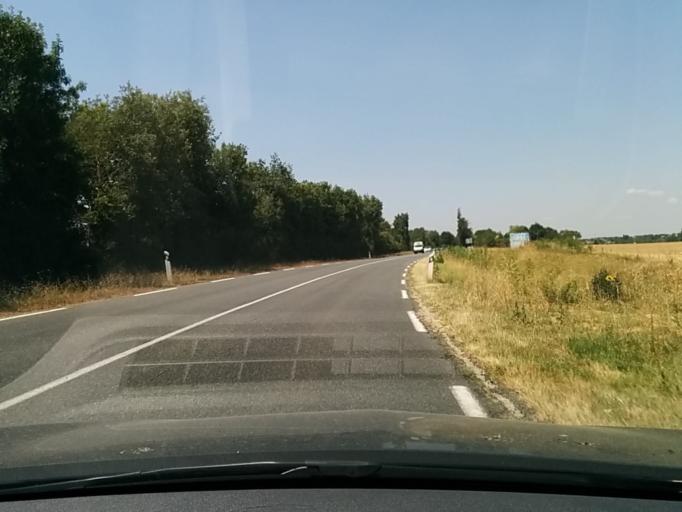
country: FR
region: Midi-Pyrenees
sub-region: Departement du Gers
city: Gimont
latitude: 43.6038
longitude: 0.9969
